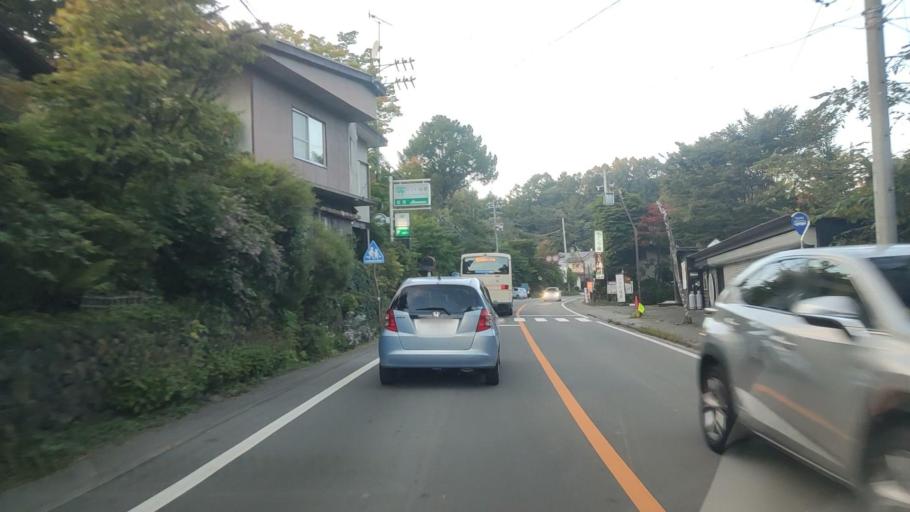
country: JP
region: Nagano
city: Komoro
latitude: 36.3545
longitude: 138.5896
